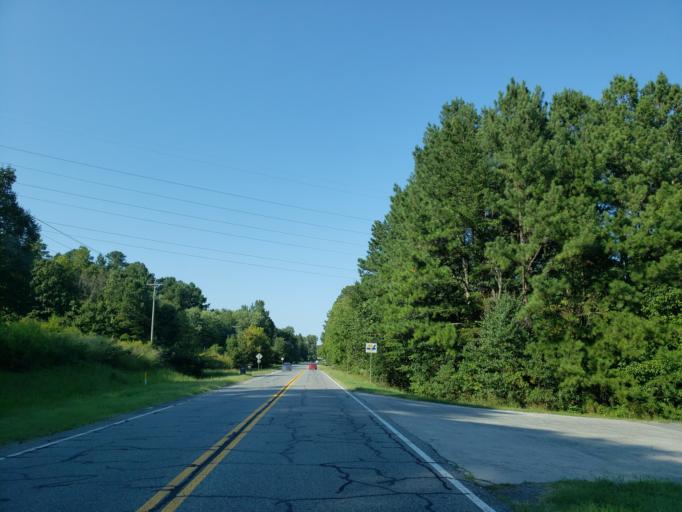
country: US
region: Georgia
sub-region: Whitfield County
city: Varnell
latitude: 34.8812
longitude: -84.9782
